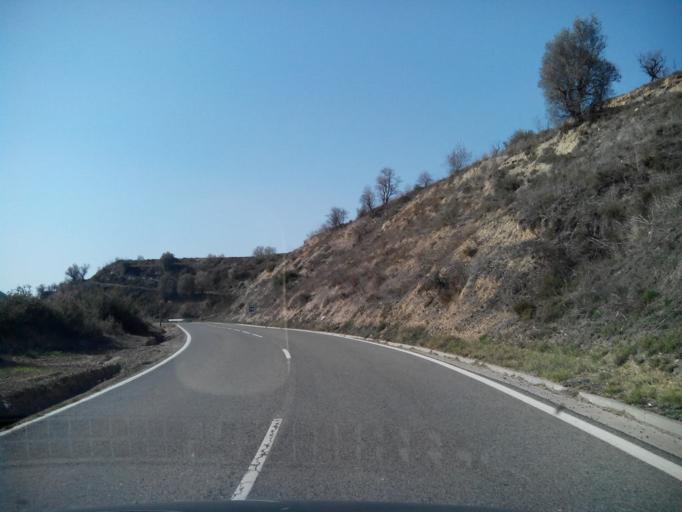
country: ES
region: Catalonia
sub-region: Provincia de Tarragona
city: Fores
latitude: 41.4540
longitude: 1.2592
